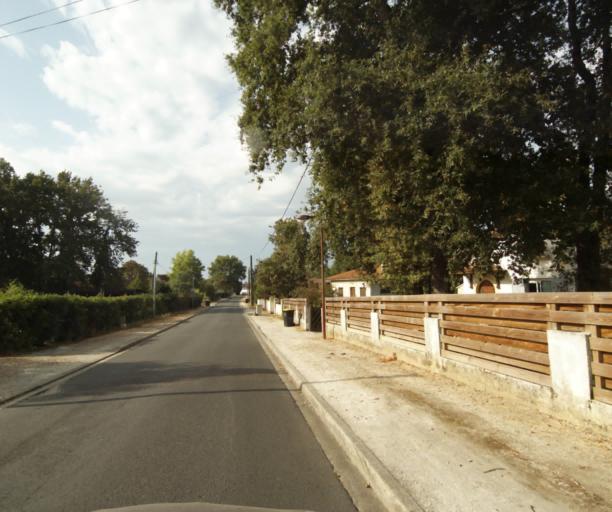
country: FR
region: Aquitaine
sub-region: Departement de la Gironde
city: Creon
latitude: 44.7652
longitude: -0.3520
